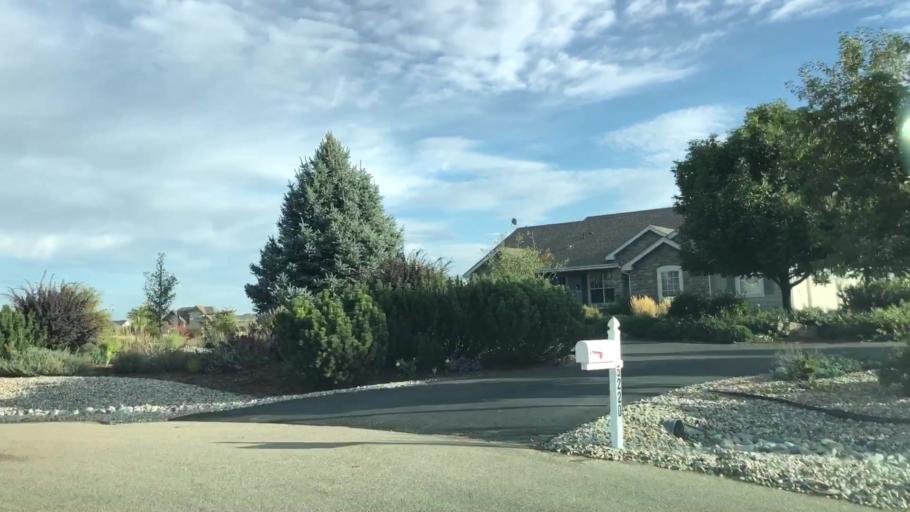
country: US
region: Colorado
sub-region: Weld County
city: Windsor
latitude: 40.4467
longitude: -104.9520
